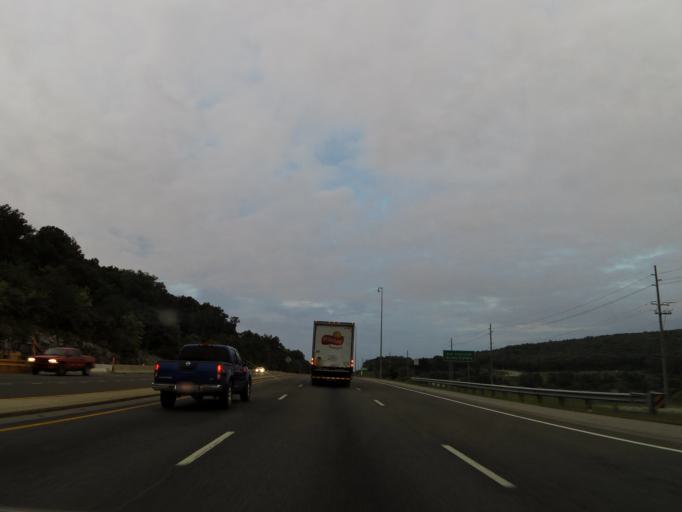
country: US
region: Alabama
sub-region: Madison County
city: Huntsville
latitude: 34.7643
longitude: -86.5569
